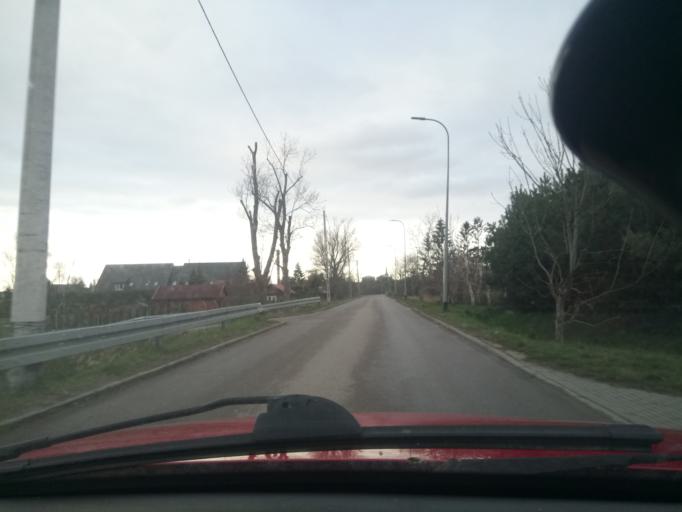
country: PL
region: Warmian-Masurian Voivodeship
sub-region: Powiat elblaski
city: Elblag
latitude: 54.1431
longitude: 19.4048
